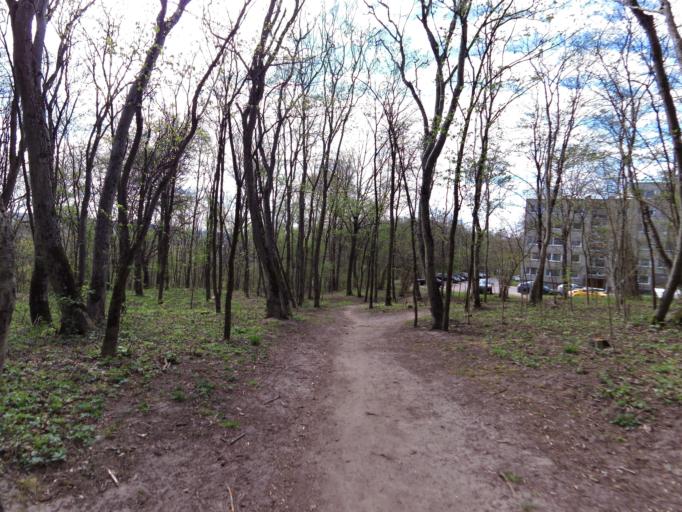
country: LT
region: Vilnius County
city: Lazdynai
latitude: 54.6835
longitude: 25.2225
